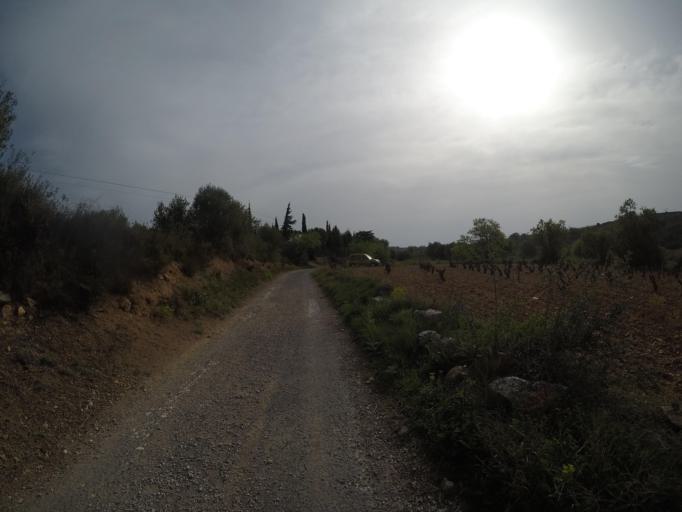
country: FR
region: Languedoc-Roussillon
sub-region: Departement des Pyrenees-Orientales
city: Baixas
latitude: 42.7455
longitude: 2.8041
